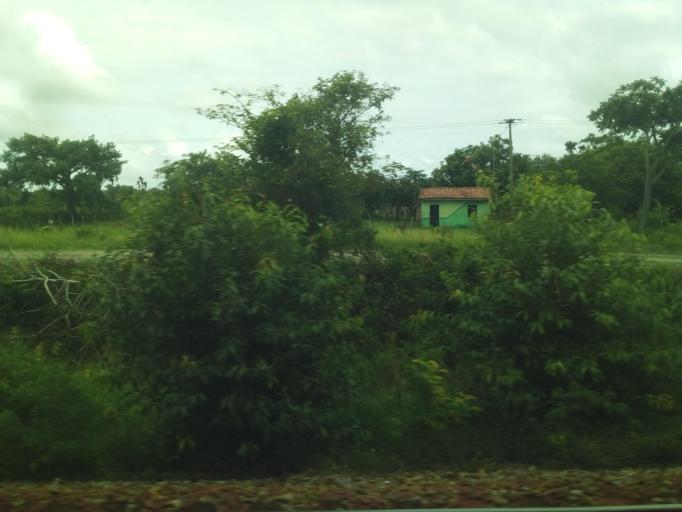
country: BR
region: Maranhao
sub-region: Arari
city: Arari
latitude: -3.5747
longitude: -44.7362
